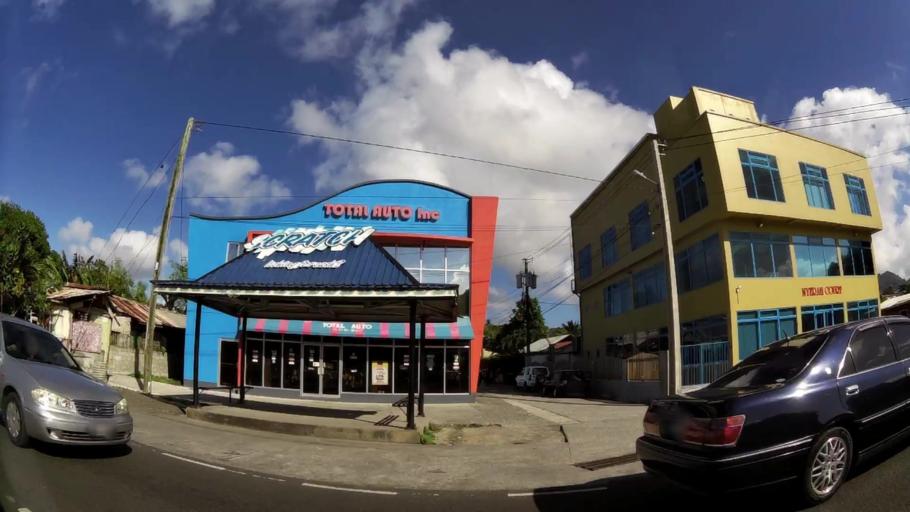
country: LC
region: Castries Quarter
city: Bisee
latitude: 14.0191
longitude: -60.9911
